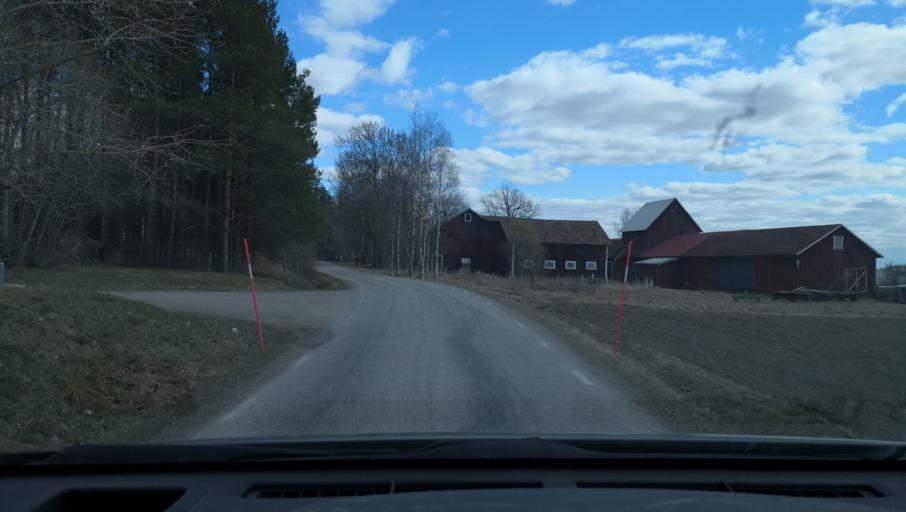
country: SE
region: Vaestmanland
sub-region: Sala Kommun
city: Sala
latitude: 59.8614
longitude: 16.5981
